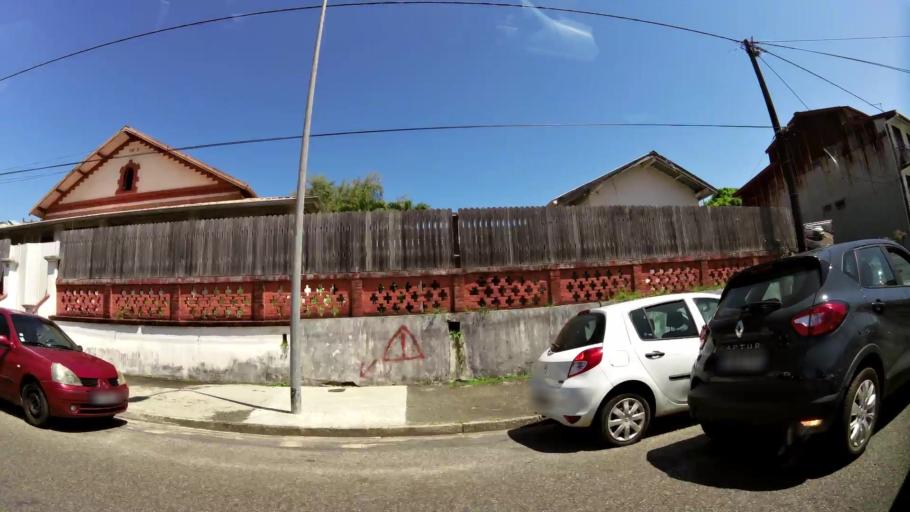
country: GF
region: Guyane
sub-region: Guyane
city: Cayenne
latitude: 4.9429
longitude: -52.3261
